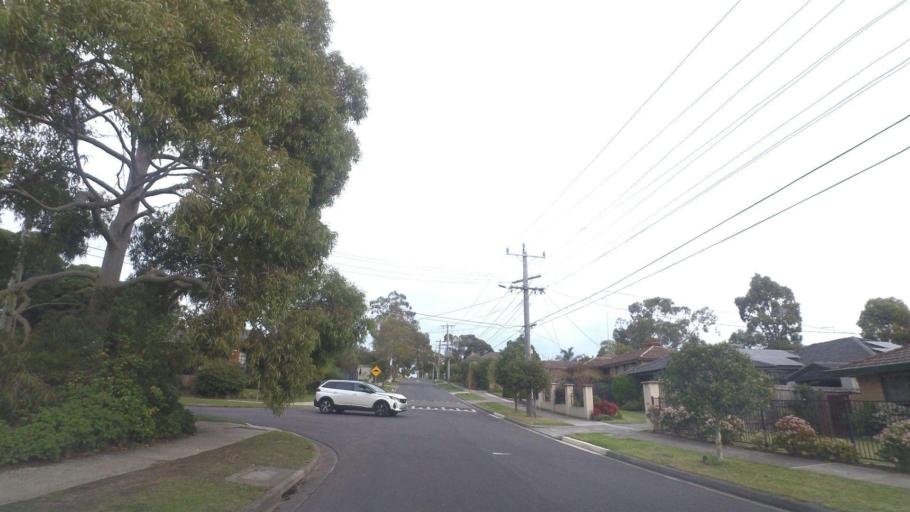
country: AU
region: Victoria
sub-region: Manningham
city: Bulleen
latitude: -37.7738
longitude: 145.0866
